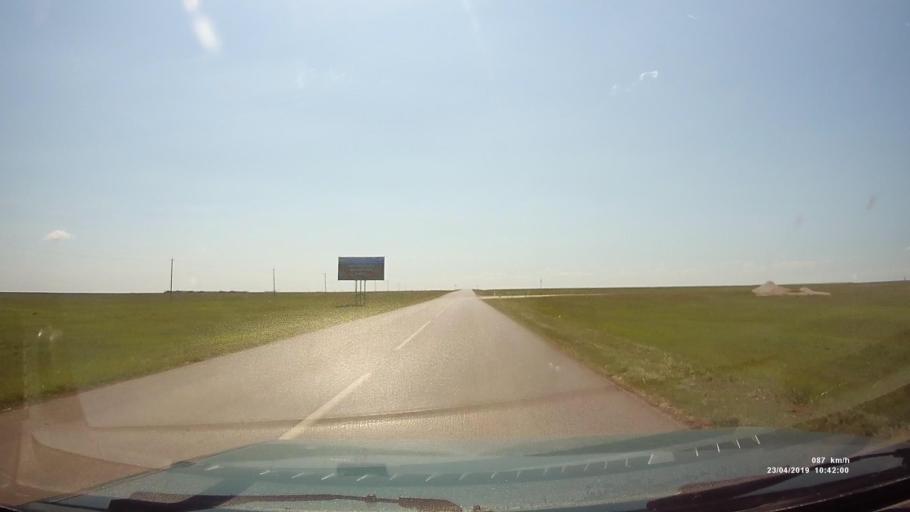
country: RU
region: Kalmykiya
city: Yashalta
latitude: 46.4877
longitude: 42.6410
